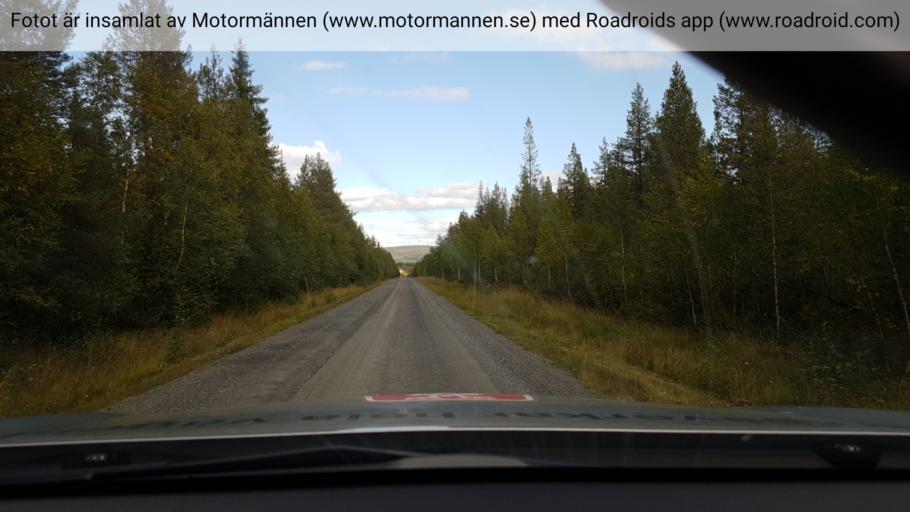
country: SE
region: Vaesterbotten
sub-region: Sorsele Kommun
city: Sorsele
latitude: 65.4591
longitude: 17.7416
